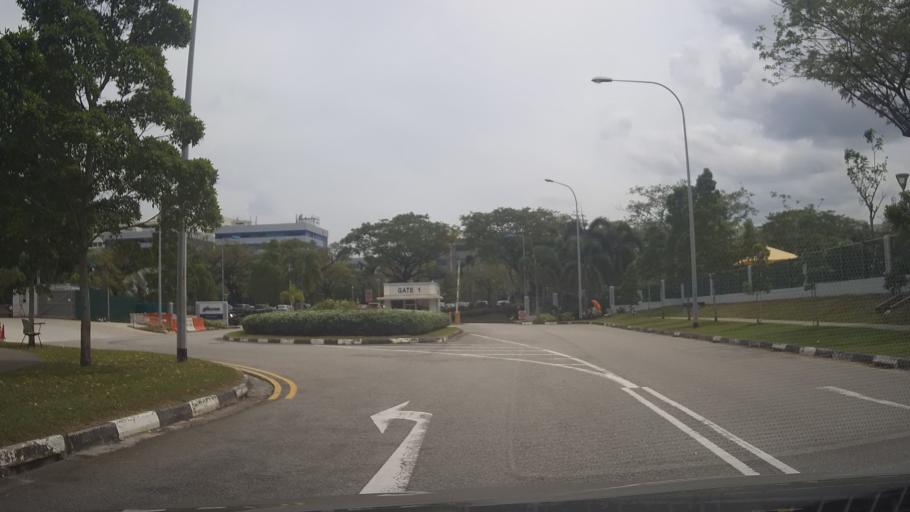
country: MY
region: Johor
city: Johor Bahru
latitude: 1.4562
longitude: 103.7950
